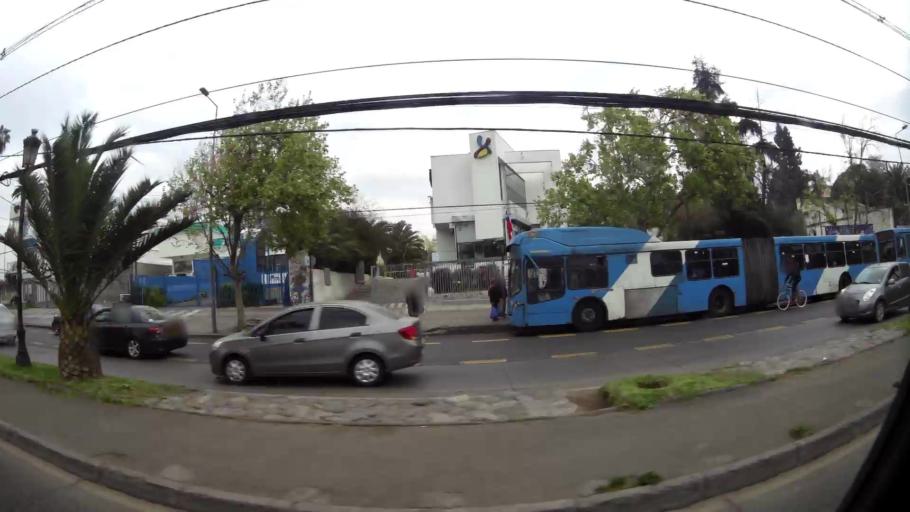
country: CL
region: Santiago Metropolitan
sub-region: Provincia de Santiago
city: Lo Prado
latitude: -33.5031
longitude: -70.7574
